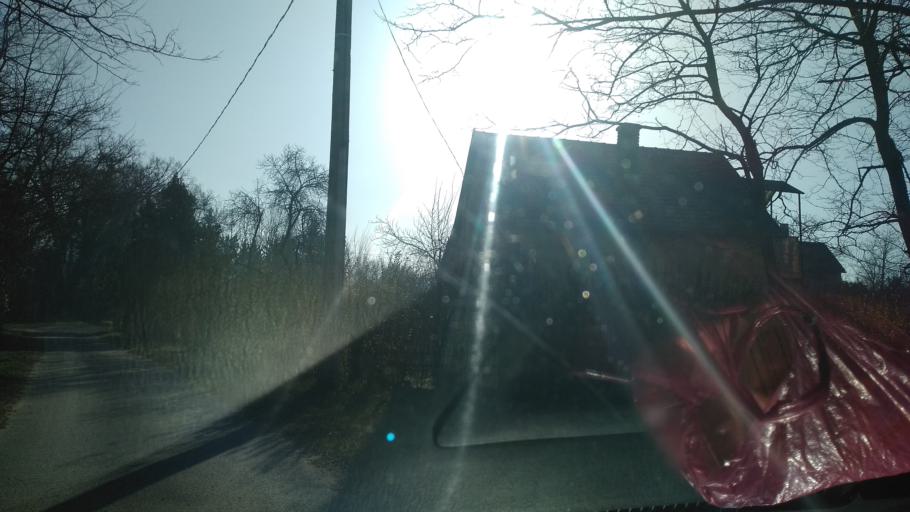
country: HU
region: Somogy
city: Barcs
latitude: 45.9546
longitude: 17.5080
